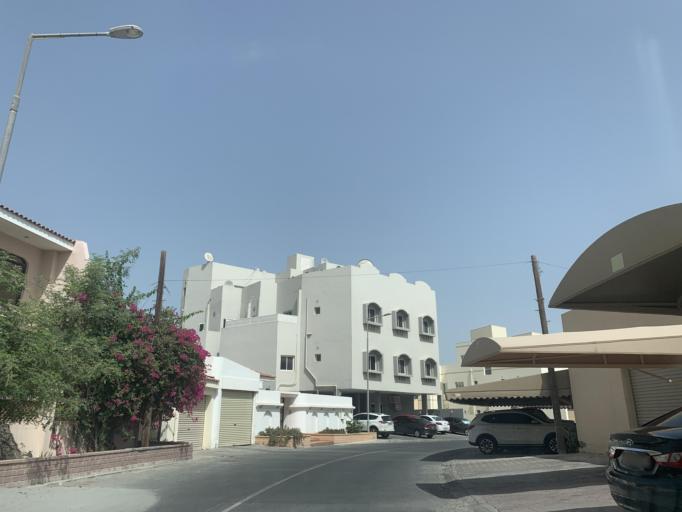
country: BH
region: Northern
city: Ar Rifa'
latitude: 26.1445
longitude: 50.5684
